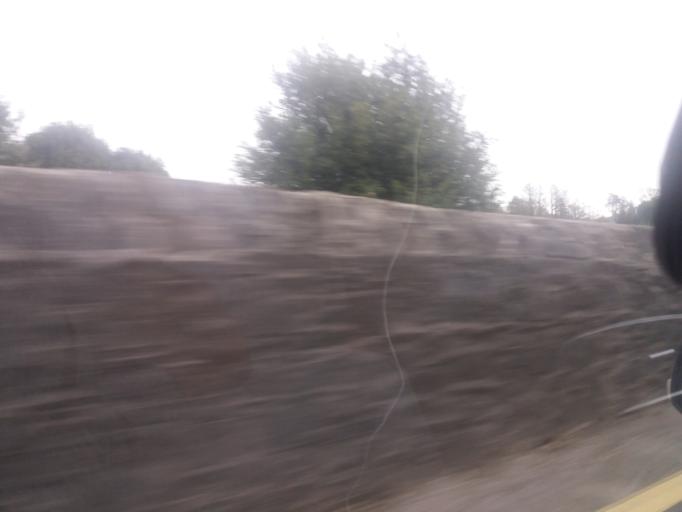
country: IE
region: Munster
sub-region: County Limerick
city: Adare
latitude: 52.5693
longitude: -8.7844
